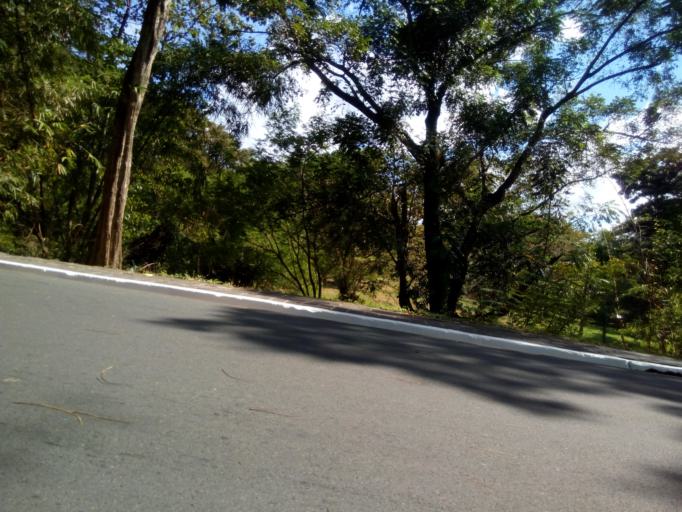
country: PH
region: Metro Manila
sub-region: Quezon City
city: Quezon City
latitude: 14.6555
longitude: 121.0685
